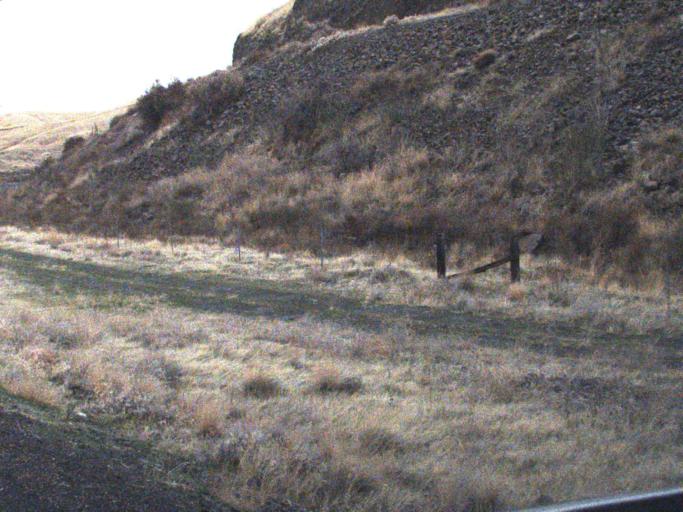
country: US
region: Washington
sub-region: Walla Walla County
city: Waitsburg
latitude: 46.5584
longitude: -118.1789
